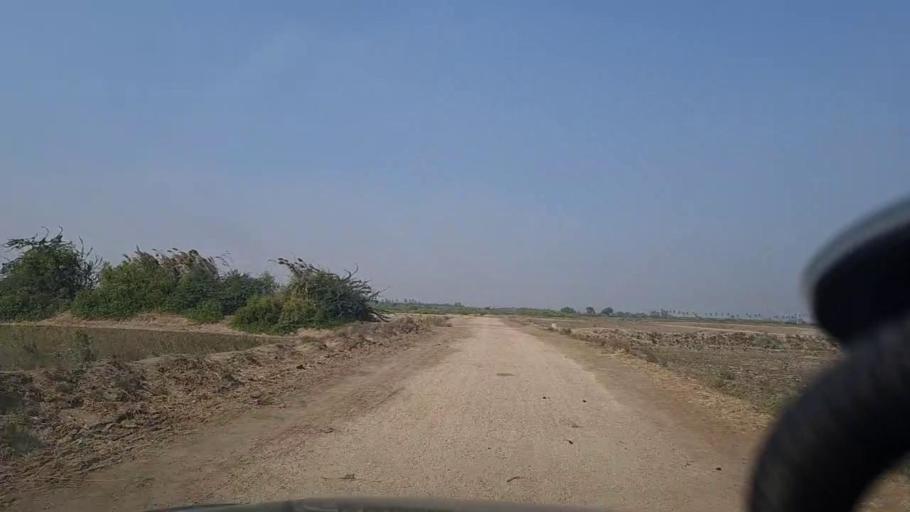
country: PK
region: Sindh
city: Thatta
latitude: 24.6186
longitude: 67.8837
